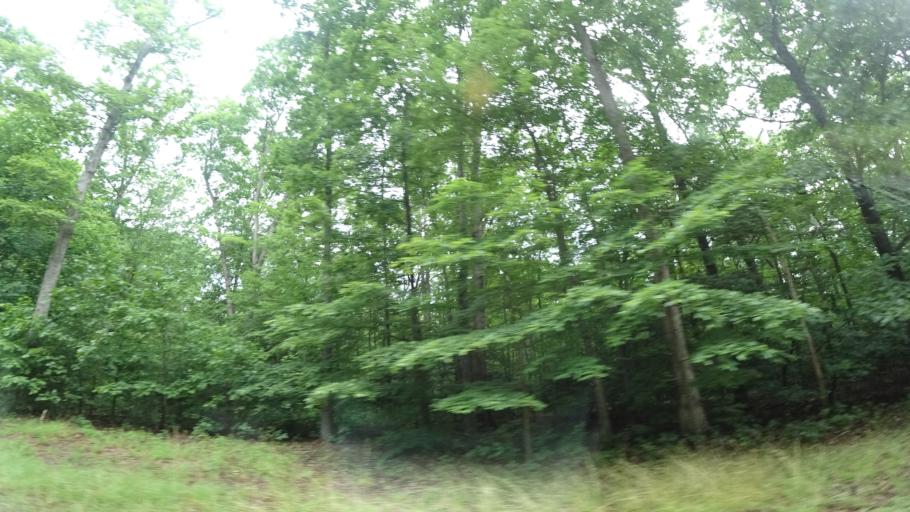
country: US
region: Virginia
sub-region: Louisa County
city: Louisa
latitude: 38.1141
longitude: -77.8163
